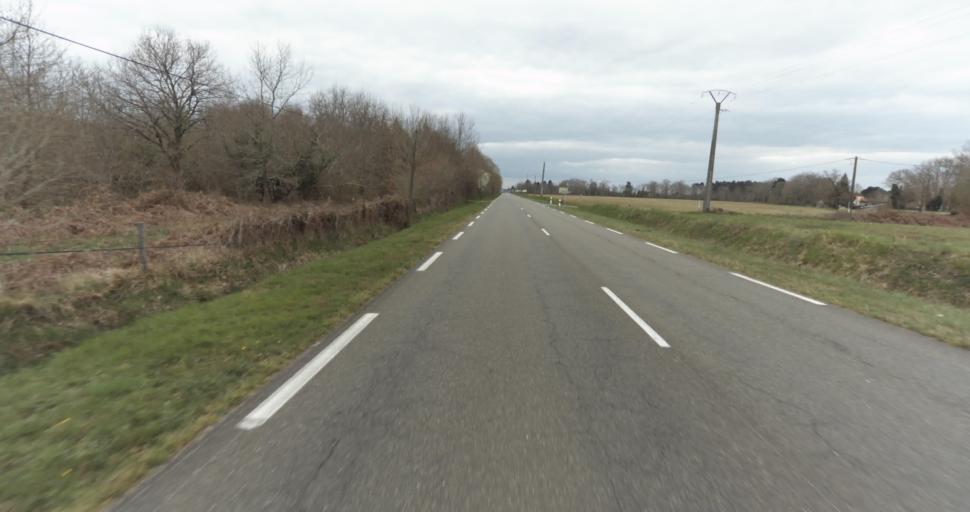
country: FR
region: Aquitaine
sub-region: Departement des Landes
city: Sarbazan
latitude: 44.0136
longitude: -0.3245
